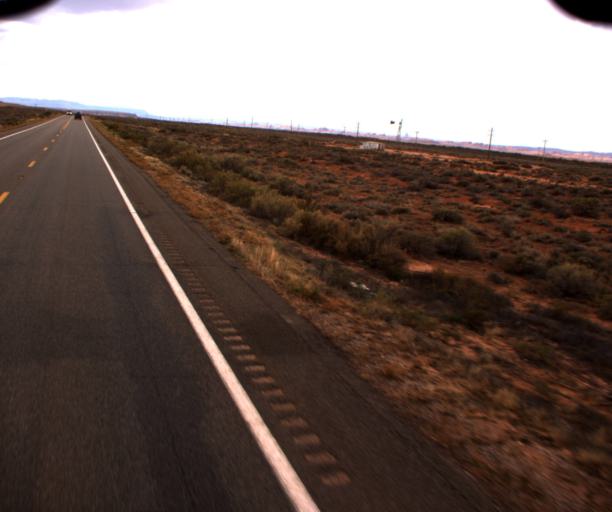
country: US
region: Arizona
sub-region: Navajo County
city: Kayenta
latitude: 36.8150
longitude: -109.8901
